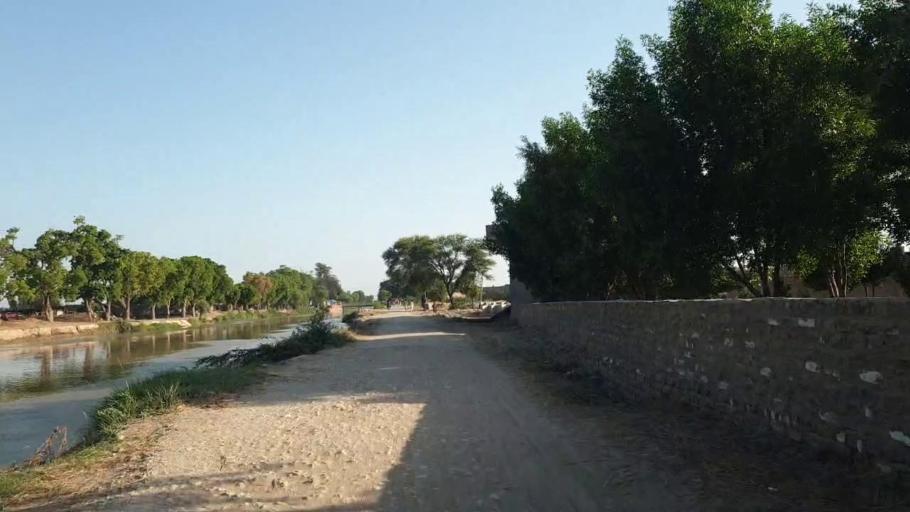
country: PK
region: Sindh
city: Hyderabad
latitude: 25.3187
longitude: 68.4285
